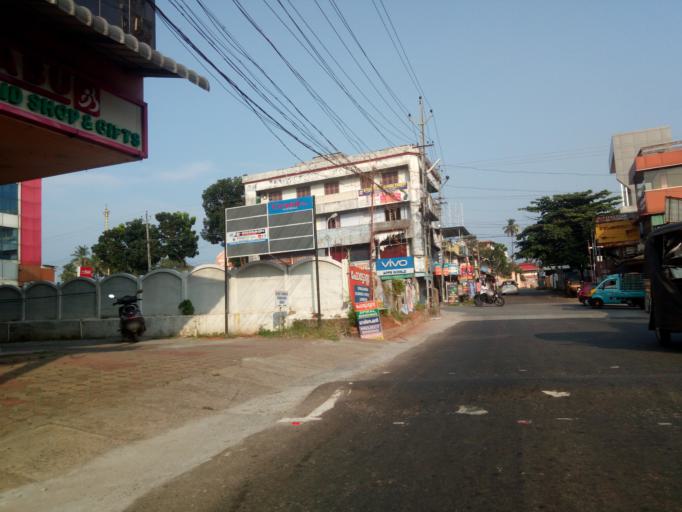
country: IN
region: Kerala
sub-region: Thrissur District
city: Irinjalakuda
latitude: 10.3432
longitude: 76.2161
